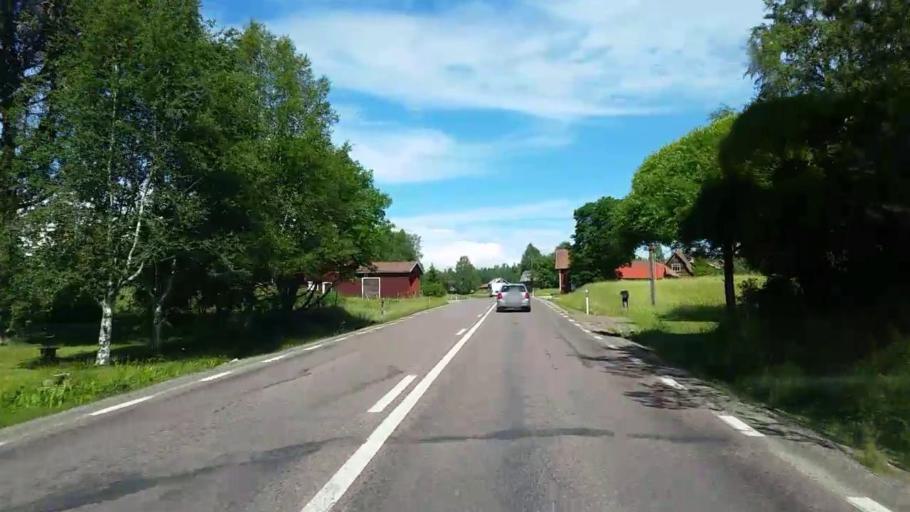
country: SE
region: Dalarna
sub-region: Rattviks Kommun
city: Raettvik
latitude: 60.9756
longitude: 15.2242
